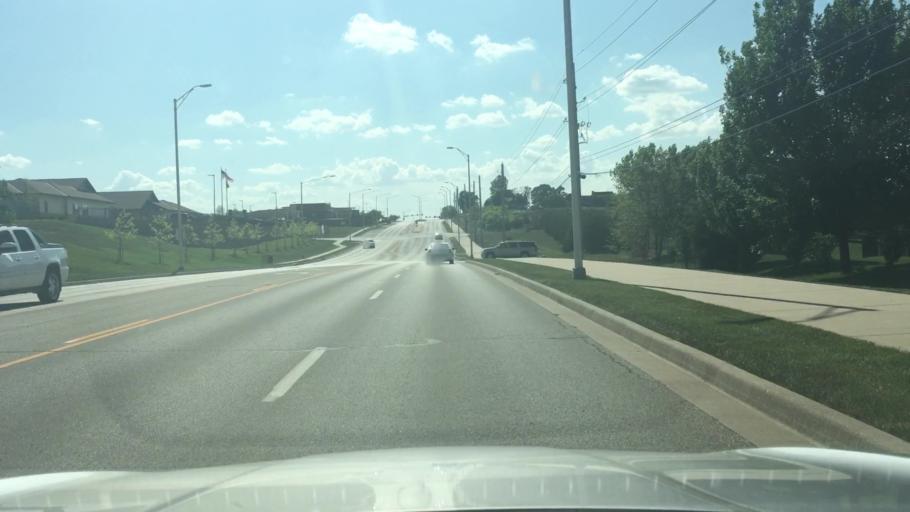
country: US
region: Missouri
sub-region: Jackson County
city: Lees Summit
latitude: 38.9130
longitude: -94.4434
